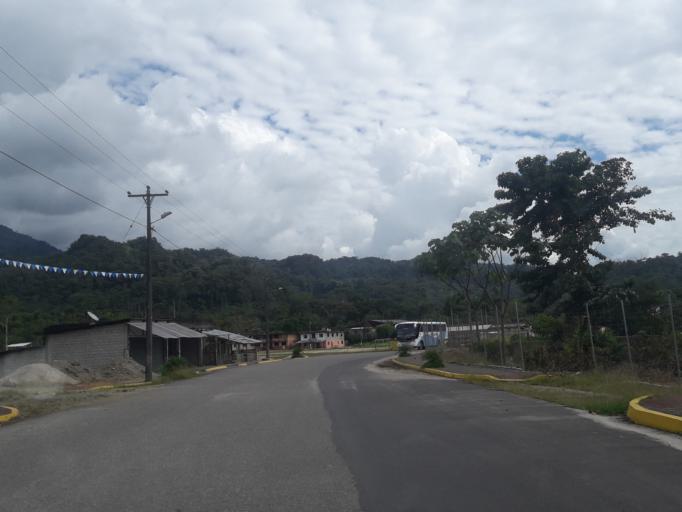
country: EC
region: Napo
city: Tena
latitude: -1.0678
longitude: -77.9074
